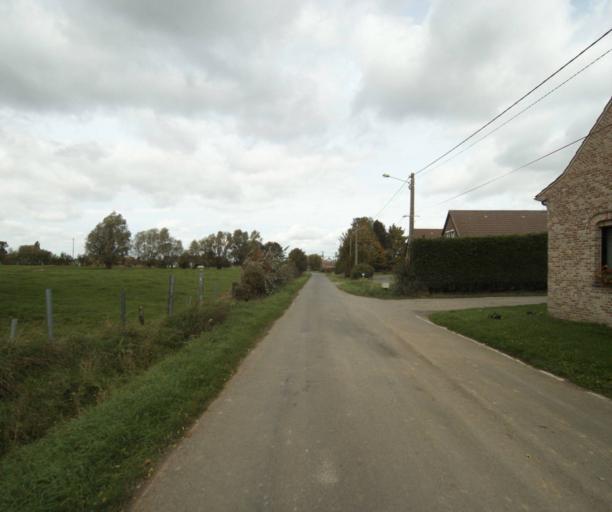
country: FR
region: Nord-Pas-de-Calais
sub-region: Departement du Nord
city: Erquinghem-Lys
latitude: 50.6666
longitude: 2.8580
